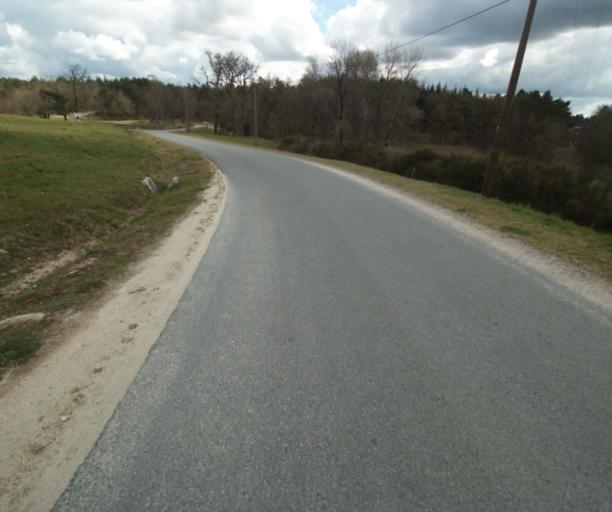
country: FR
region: Limousin
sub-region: Departement de la Correze
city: Correze
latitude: 45.3118
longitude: 1.9317
